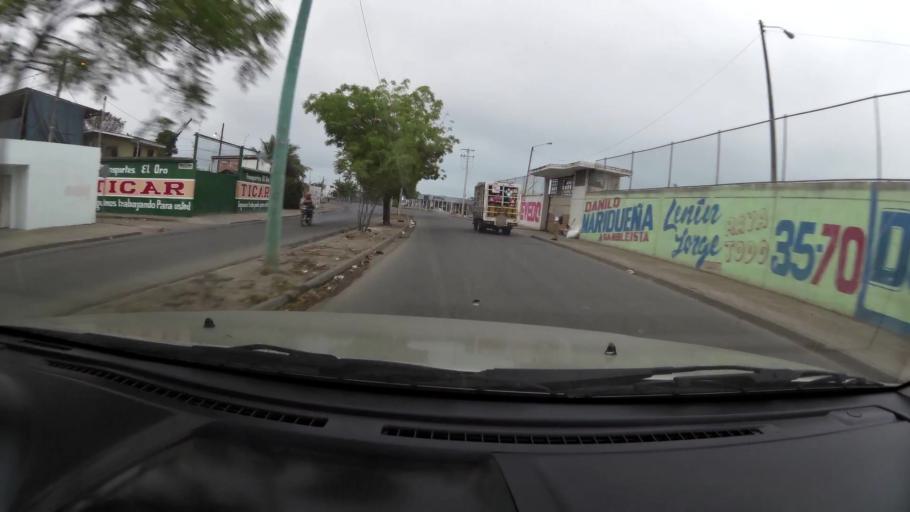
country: EC
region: El Oro
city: Machala
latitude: -3.2560
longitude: -79.9404
